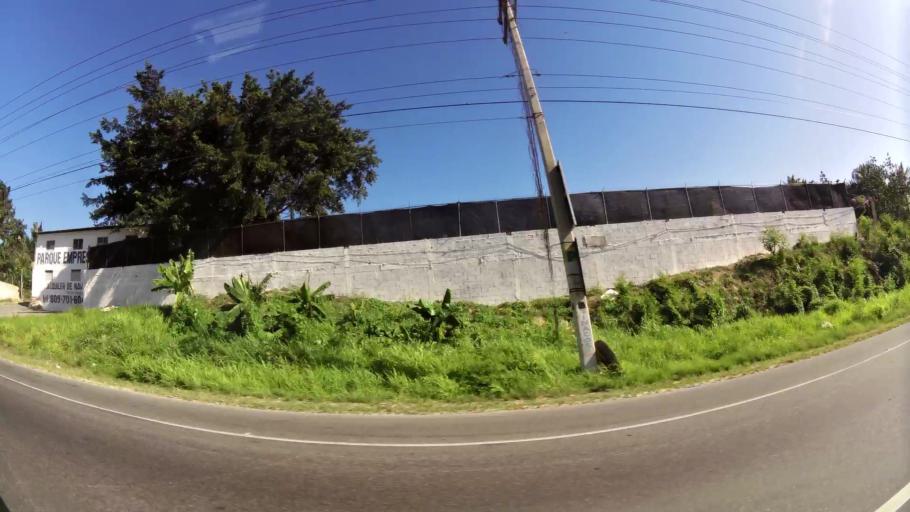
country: DO
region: San Cristobal
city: San Cristobal
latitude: 18.4343
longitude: -70.0786
